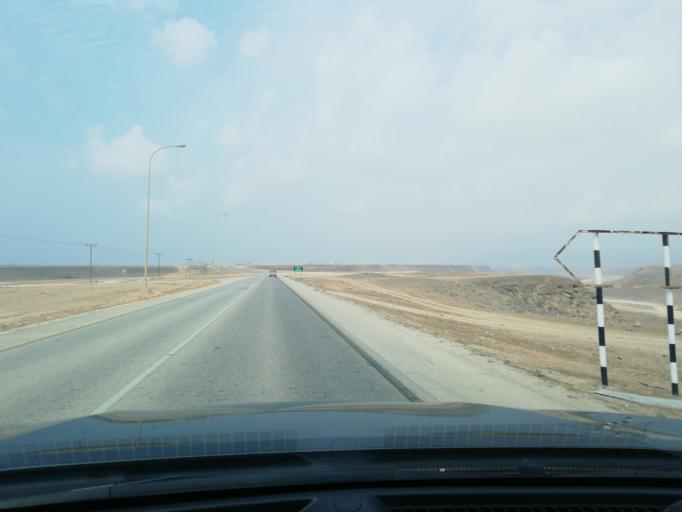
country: OM
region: Zufar
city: Salalah
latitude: 16.9512
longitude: 53.8573
